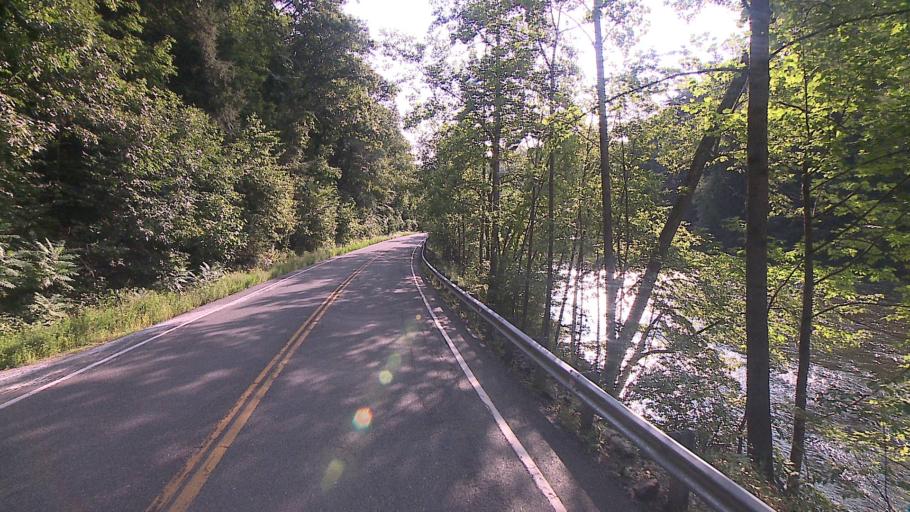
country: US
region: Connecticut
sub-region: Litchfield County
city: Canaan
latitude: 41.8689
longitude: -73.3676
